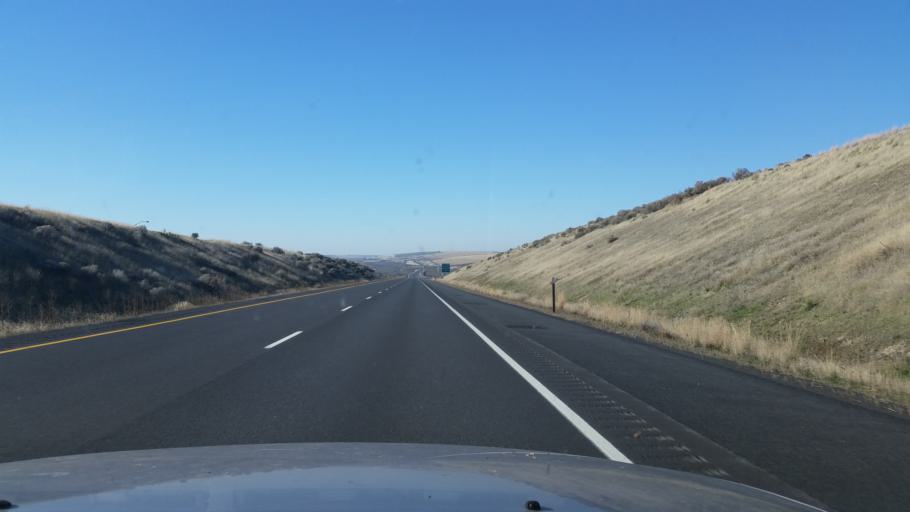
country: US
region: Washington
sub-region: Grant County
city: Warden
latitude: 47.0872
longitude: -118.8641
